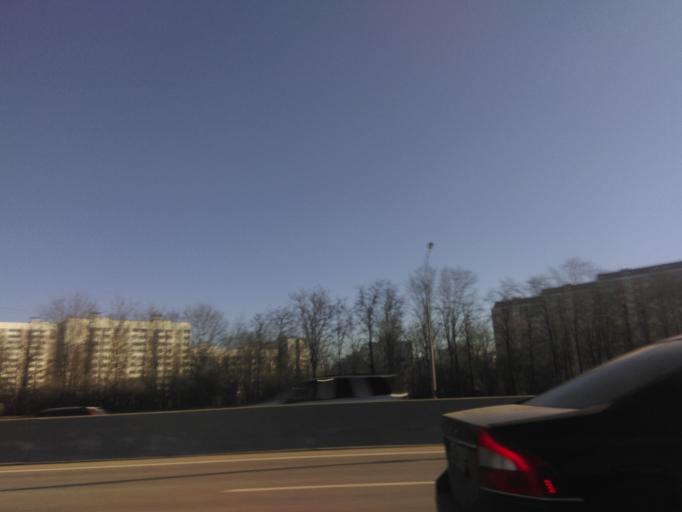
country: RU
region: Moskovskaya
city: Marfino
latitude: 55.7070
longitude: 37.3917
